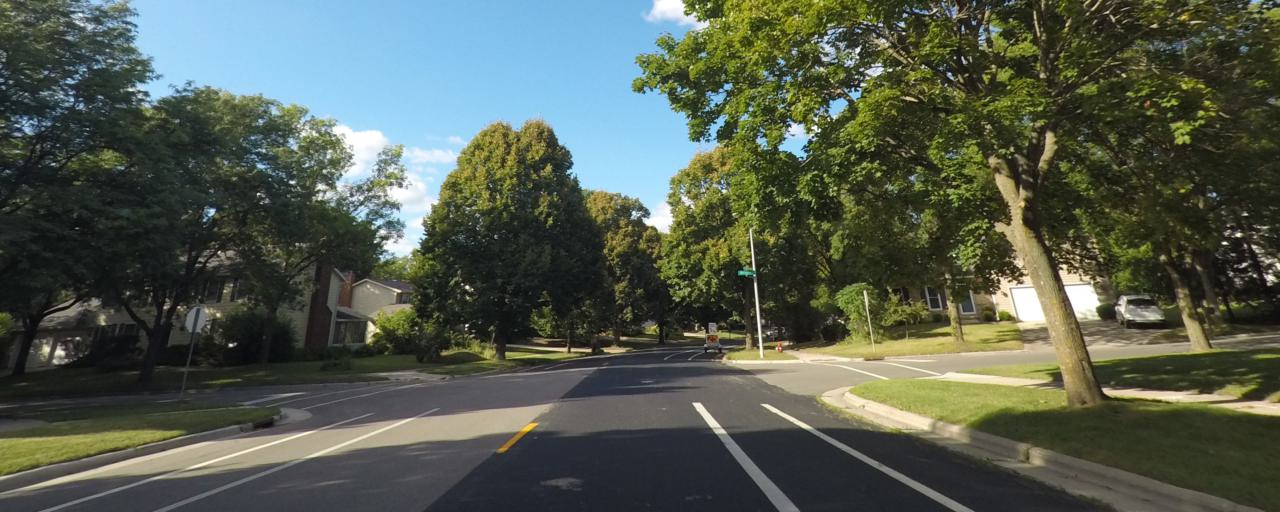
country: US
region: Wisconsin
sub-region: Dane County
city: Middleton
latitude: 43.0721
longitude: -89.5104
